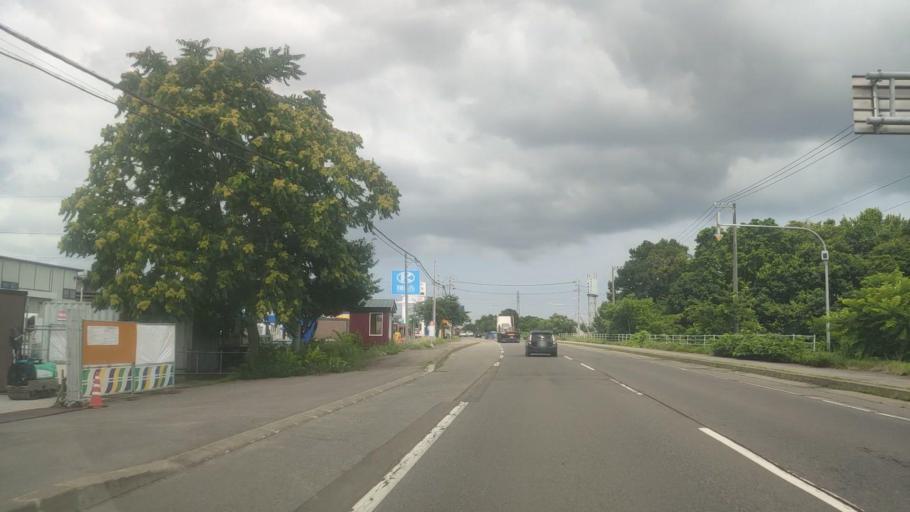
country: JP
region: Hokkaido
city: Nanae
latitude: 42.0888
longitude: 140.5818
